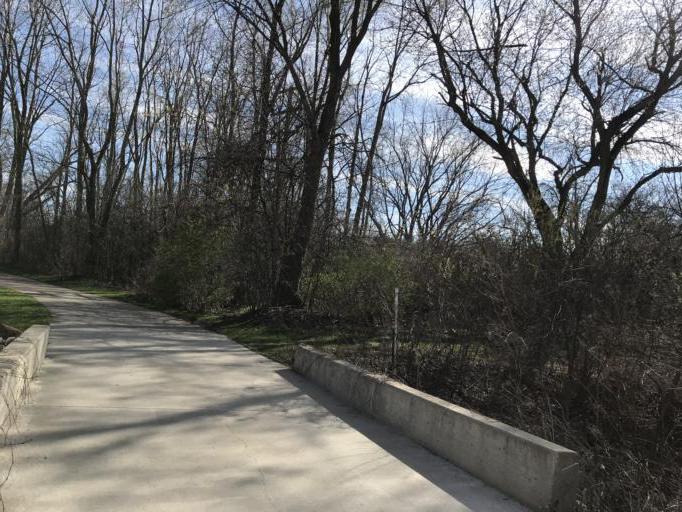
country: US
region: Michigan
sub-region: Washtenaw County
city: Ann Arbor
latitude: 42.2569
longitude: -83.7024
